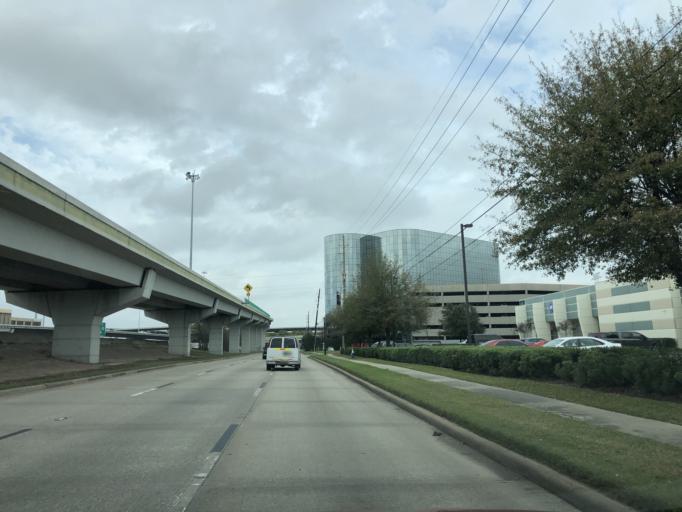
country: US
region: Texas
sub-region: Harris County
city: Aldine
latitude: 29.9354
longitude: -95.4116
